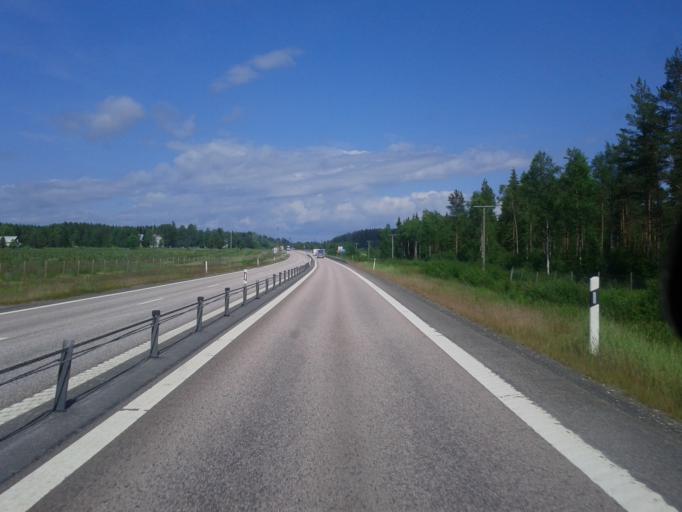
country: SE
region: Vaesternorrland
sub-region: OErnskoeldsviks Kommun
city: Husum
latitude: 63.4120
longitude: 19.2060
